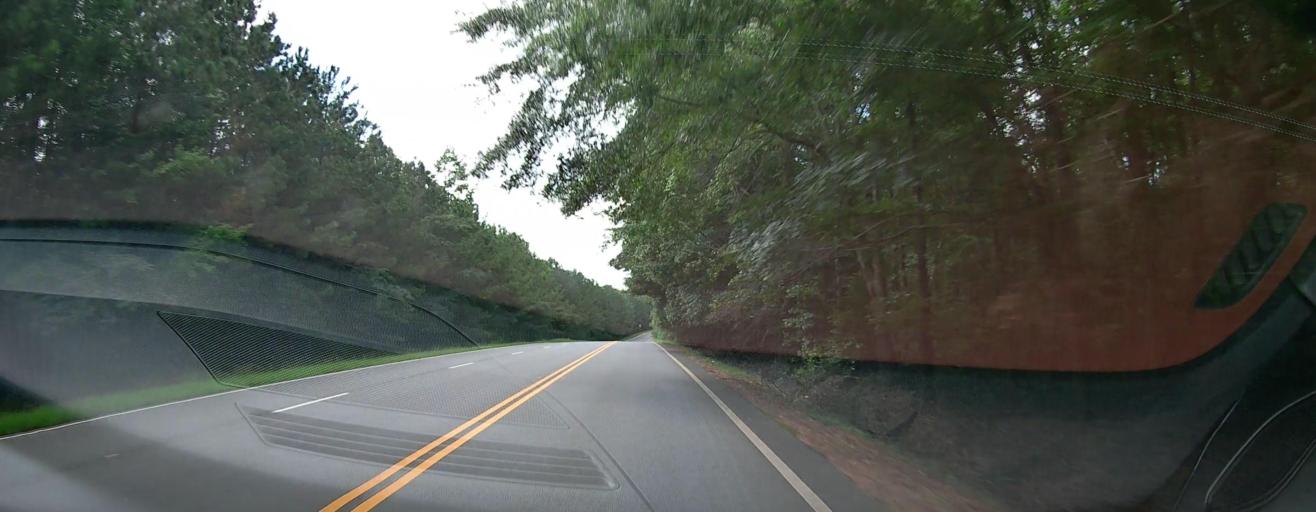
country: US
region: Georgia
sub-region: Bibb County
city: West Point
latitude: 32.8727
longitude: -83.9178
